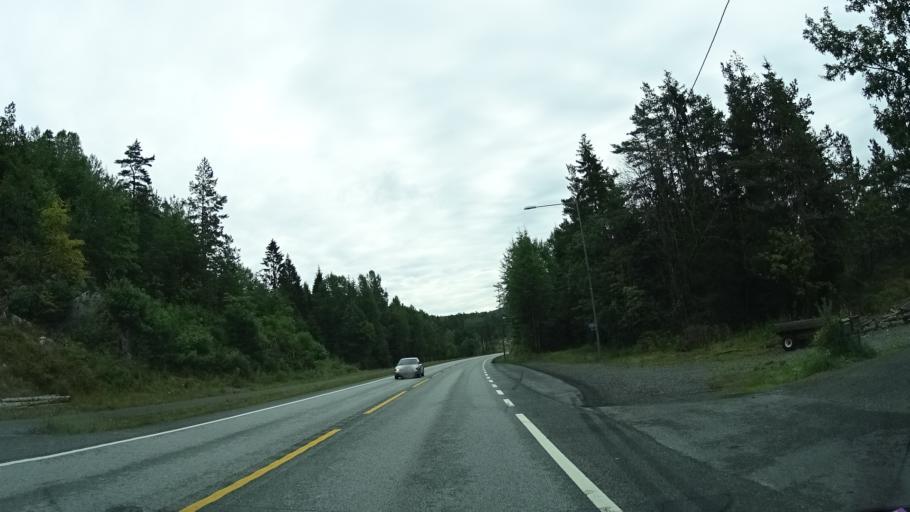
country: NO
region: Aust-Agder
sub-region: Tvedestrand
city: Tvedestrand
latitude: 58.5725
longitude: 8.8339
